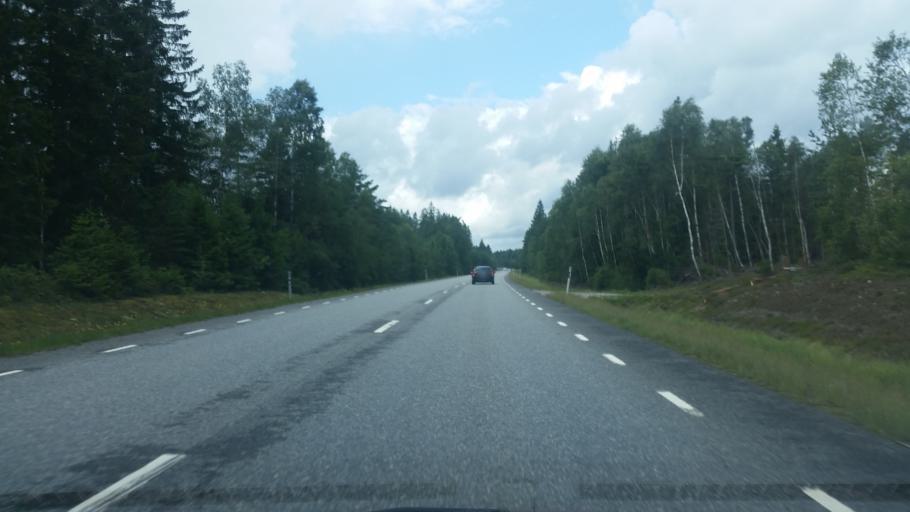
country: SE
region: Vaestra Goetaland
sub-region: Tranemo Kommun
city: Langhem
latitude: 57.5935
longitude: 13.1920
